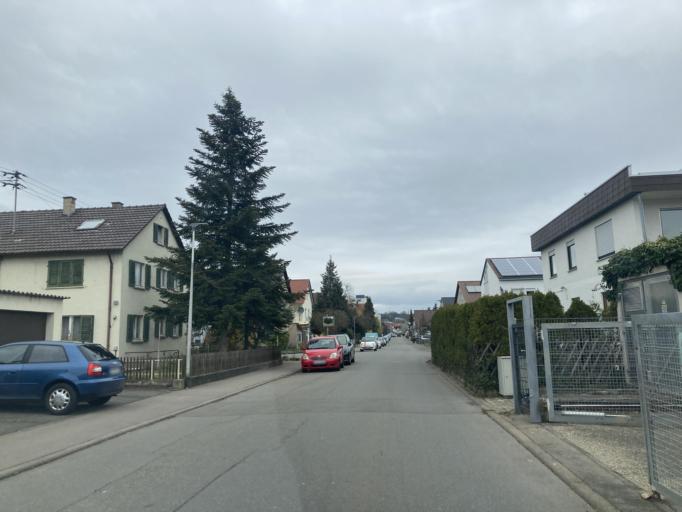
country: DE
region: Baden-Wuerttemberg
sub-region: Tuebingen Region
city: Rottenburg
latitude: 48.4757
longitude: 8.9471
